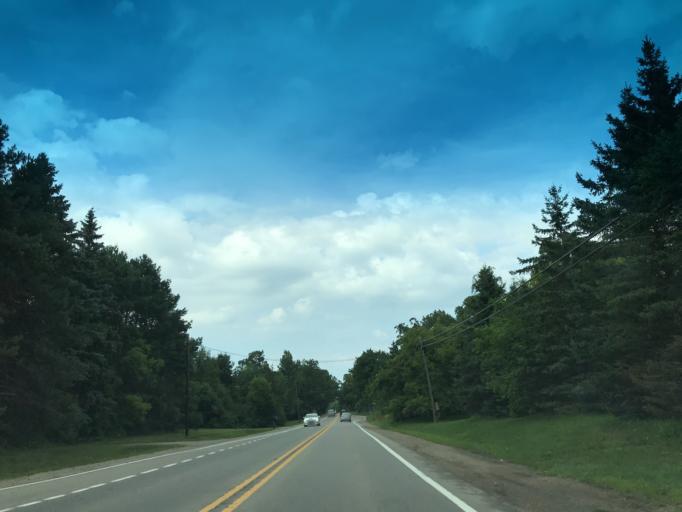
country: US
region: Michigan
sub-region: Oakland County
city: Milford
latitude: 42.5689
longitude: -83.6151
